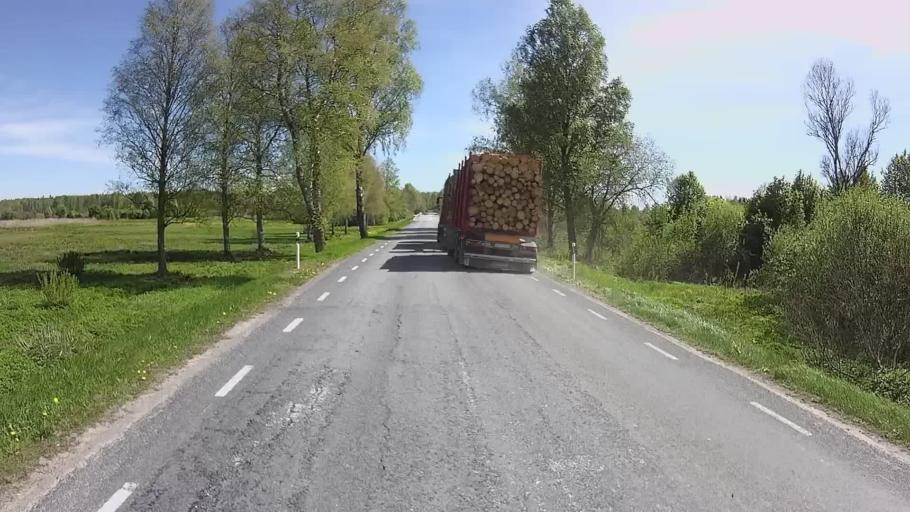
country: LV
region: Apes Novads
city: Ape
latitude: 57.6194
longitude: 26.6026
